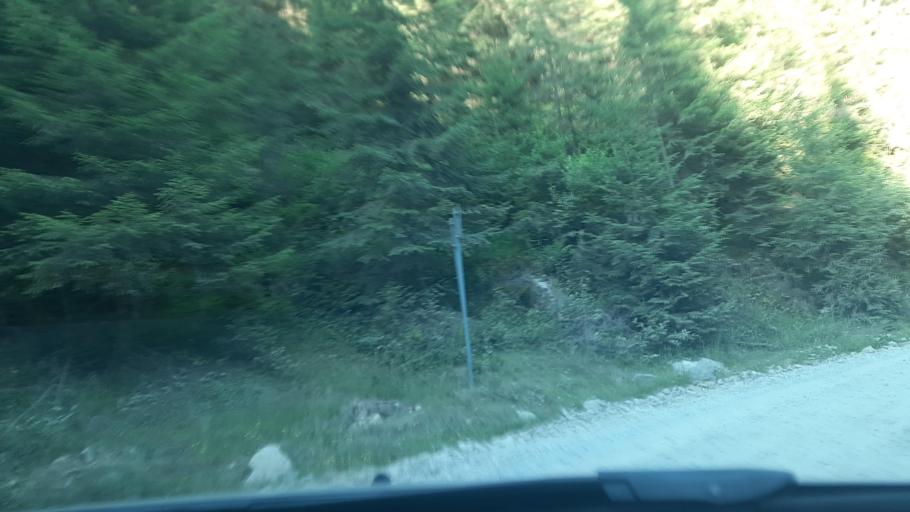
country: RO
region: Alba
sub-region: Comuna Sugag
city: Sugag
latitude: 45.5775
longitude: 23.6051
